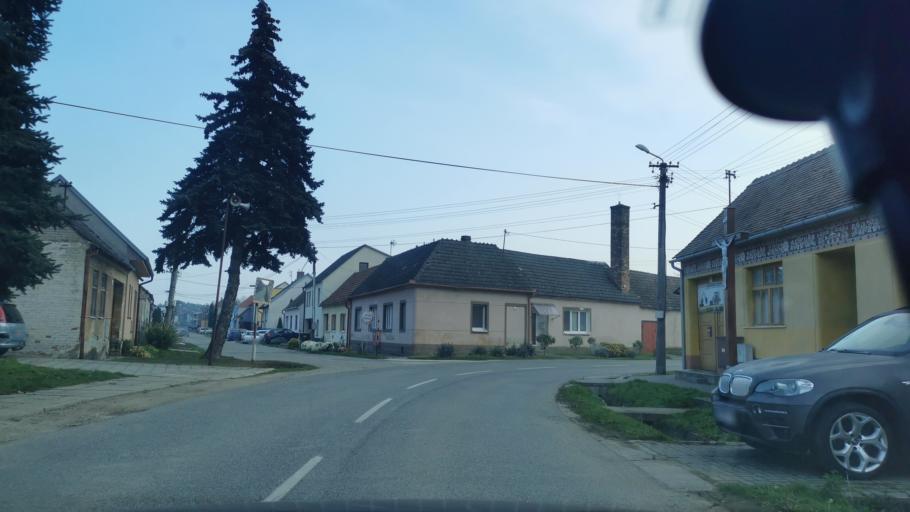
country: SK
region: Trnavsky
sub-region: Okres Skalica
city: Skalica
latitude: 48.7717
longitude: 17.2818
